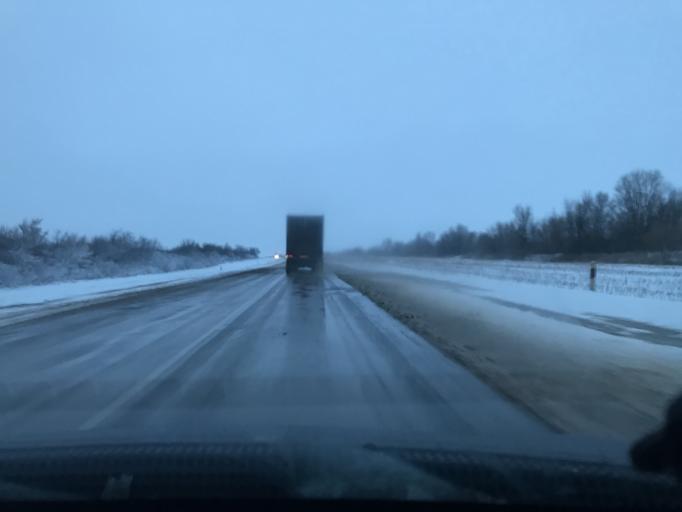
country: RU
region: Rostov
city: Letnik
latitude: 46.0153
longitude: 41.2112
